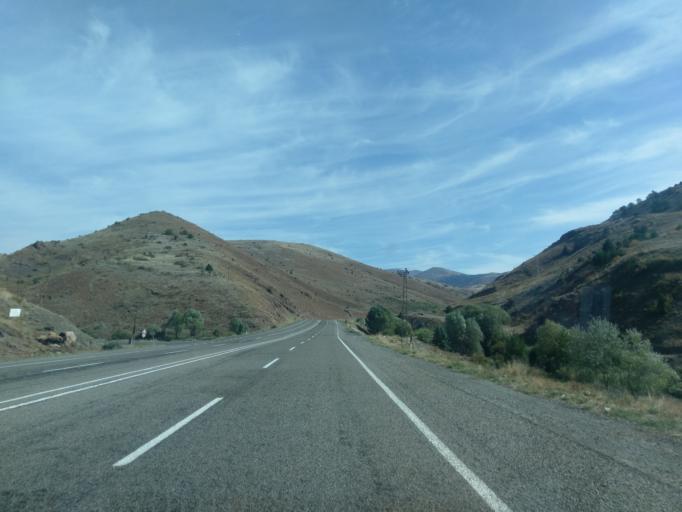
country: TR
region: Sivas
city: Imranli
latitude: 39.8511
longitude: 38.2955
